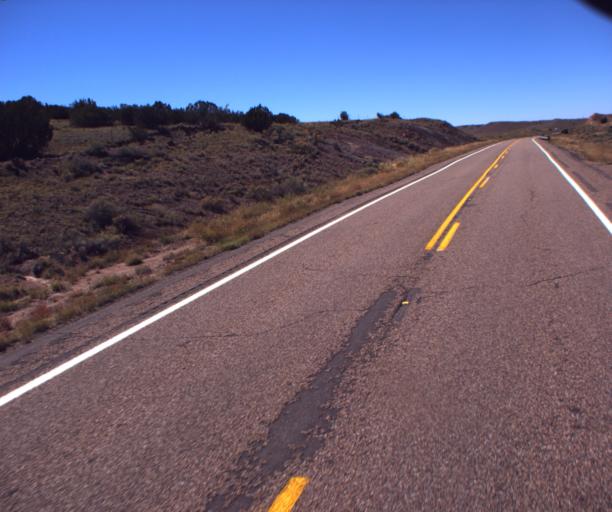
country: US
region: Arizona
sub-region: Apache County
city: Saint Johns
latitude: 34.5861
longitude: -109.5603
